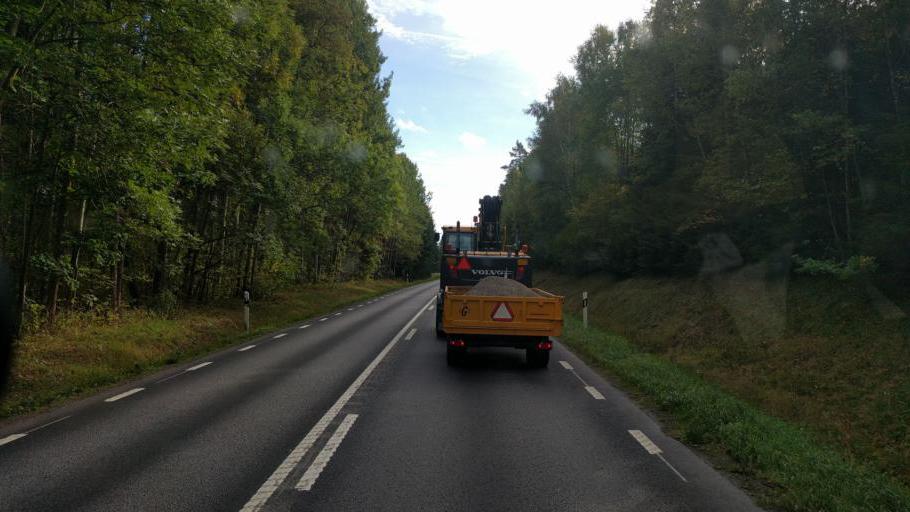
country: SE
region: OEstergoetland
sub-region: Kinda Kommun
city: Kisa
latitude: 57.9679
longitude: 15.6537
